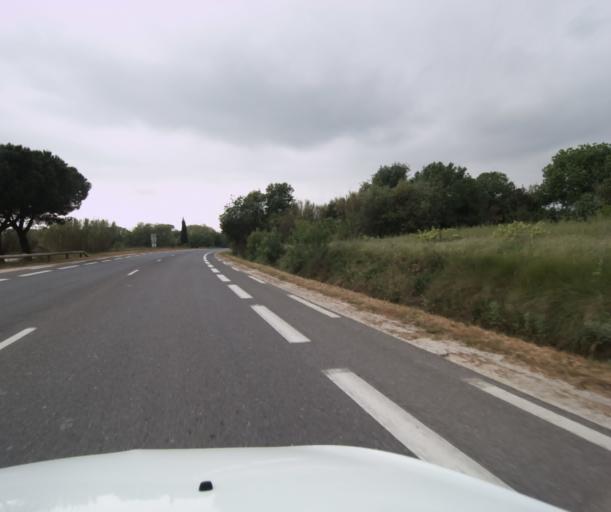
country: FR
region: Provence-Alpes-Cote d'Azur
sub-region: Departement du Var
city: La Crau
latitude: 43.1262
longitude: 6.0862
